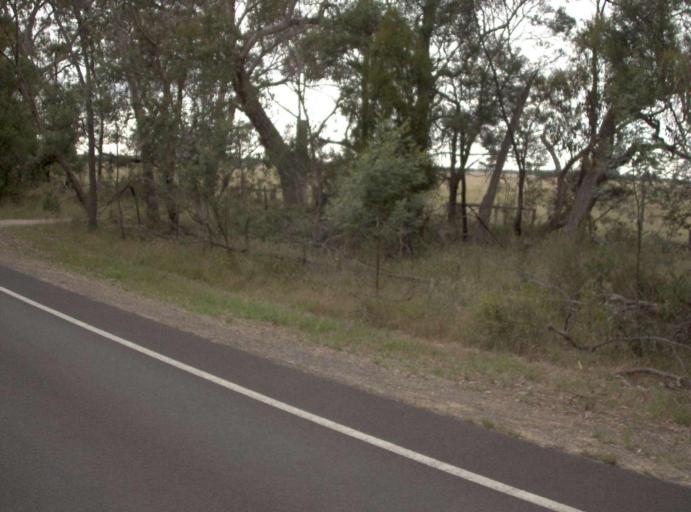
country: AU
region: Victoria
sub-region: Wellington
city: Sale
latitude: -38.4113
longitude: 146.9633
